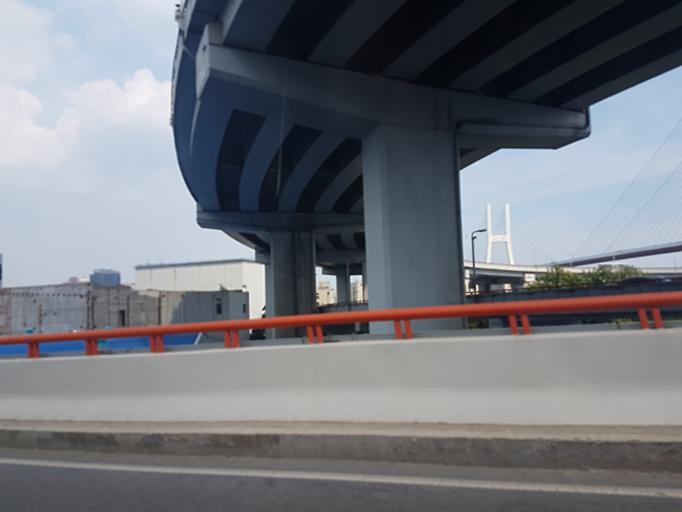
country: CN
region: Shanghai Shi
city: Luwan
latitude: 31.2113
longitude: 121.4970
